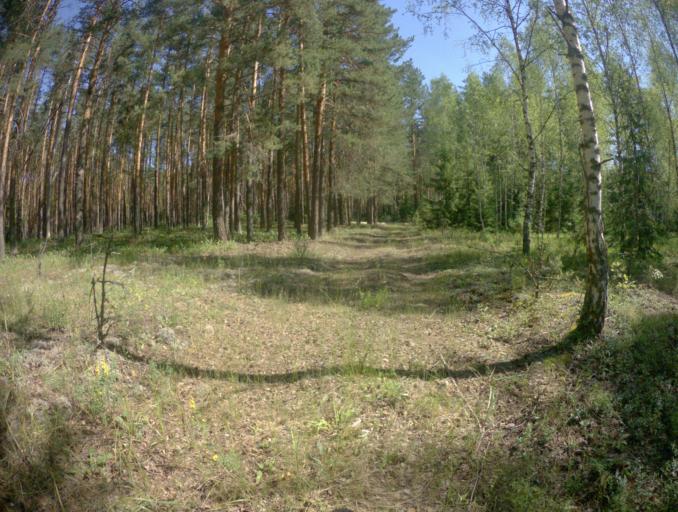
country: RU
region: Ivanovo
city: Talitsy
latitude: 56.3385
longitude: 42.3263
